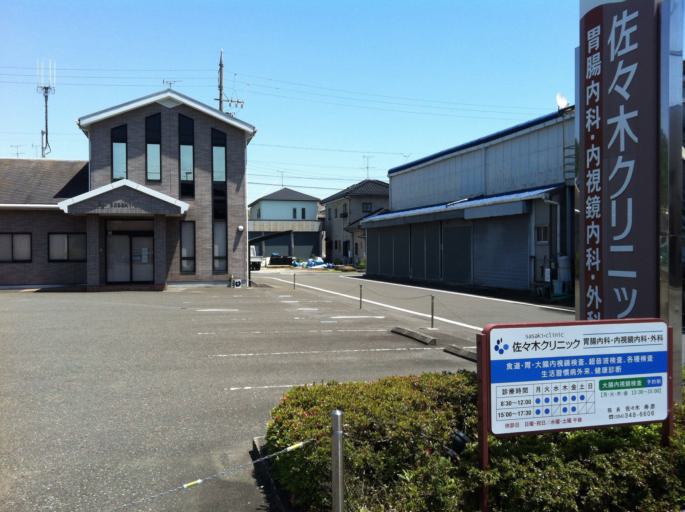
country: JP
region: Shizuoka
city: Shizuoka-shi
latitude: 35.0372
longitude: 138.4556
